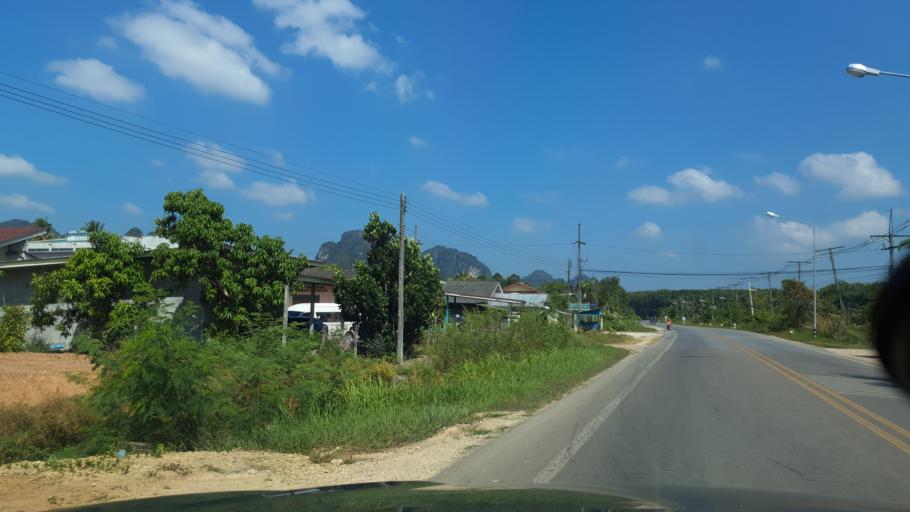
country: TH
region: Phangnga
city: Ban Ao Nang
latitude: 8.0598
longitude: 98.8592
